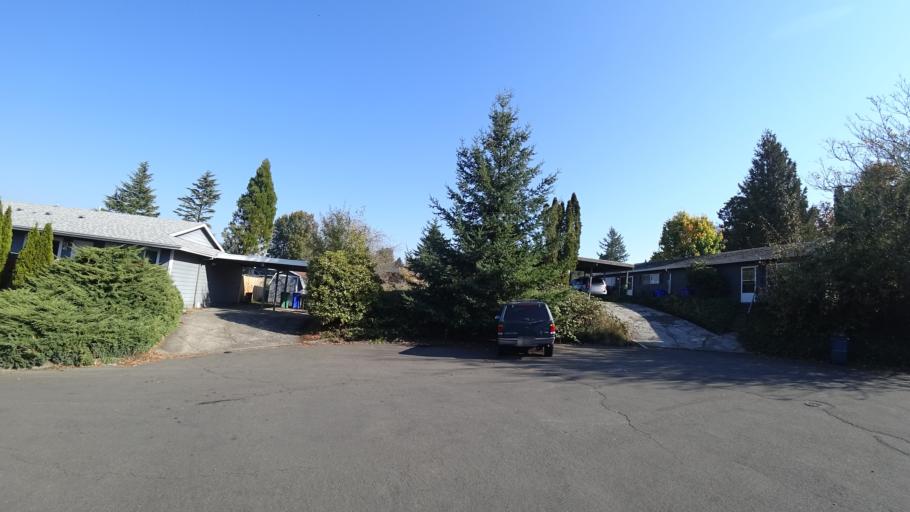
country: US
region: Oregon
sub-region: Multnomah County
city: Gresham
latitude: 45.5038
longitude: -122.4542
